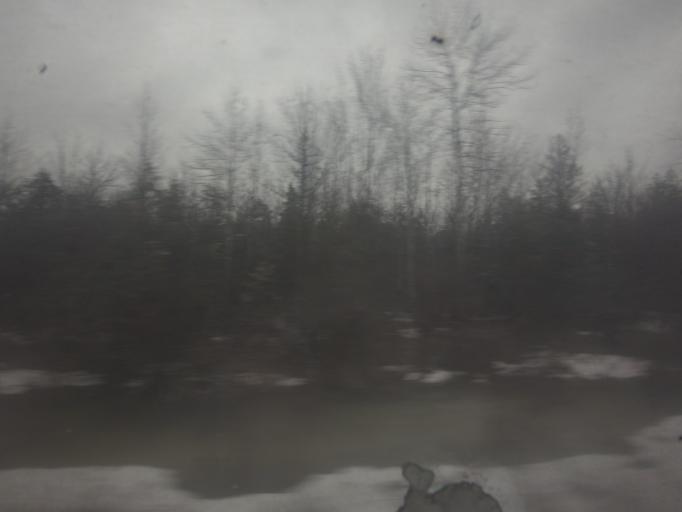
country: CA
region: Ontario
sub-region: Lanark County
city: Smiths Falls
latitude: 45.0544
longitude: -75.9168
